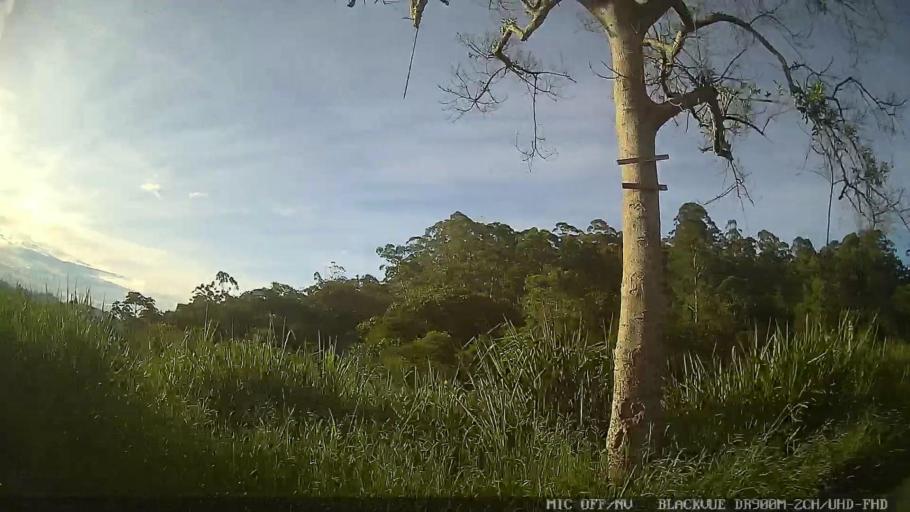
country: BR
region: Sao Paulo
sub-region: Mogi das Cruzes
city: Mogi das Cruzes
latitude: -23.5201
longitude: -46.1452
